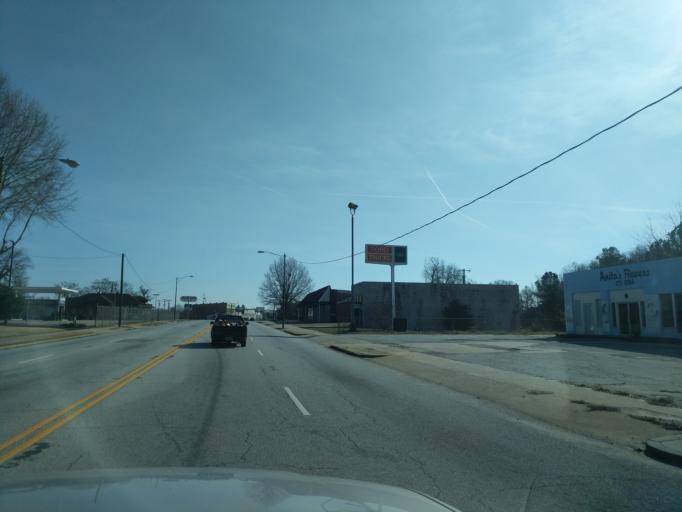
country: US
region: South Carolina
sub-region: Spartanburg County
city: Woodruff
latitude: 34.7421
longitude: -82.0395
